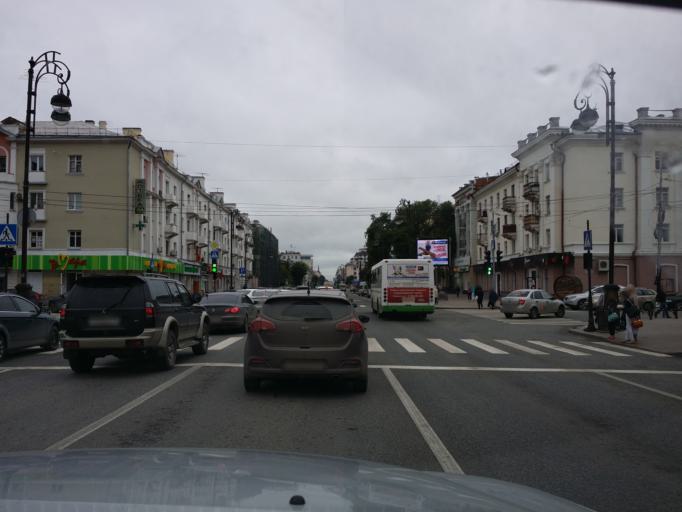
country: RU
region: Tjumen
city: Tyumen
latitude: 57.1510
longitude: 65.5447
